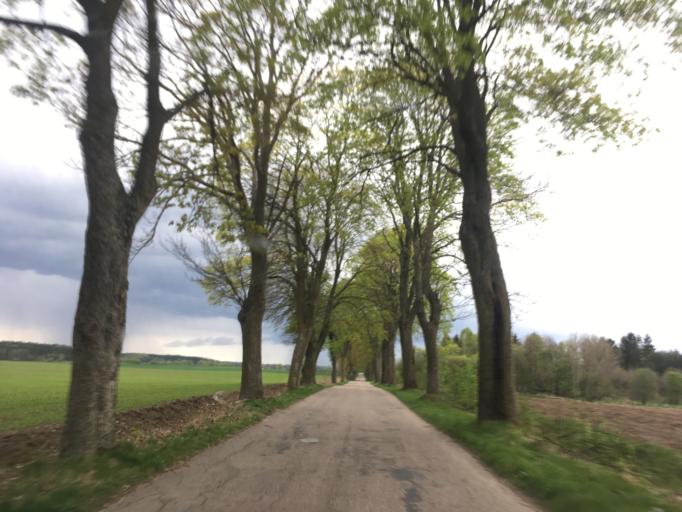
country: PL
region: Warmian-Masurian Voivodeship
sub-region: Powiat ostrodzki
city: Dabrowno
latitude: 53.4137
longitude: 20.0948
